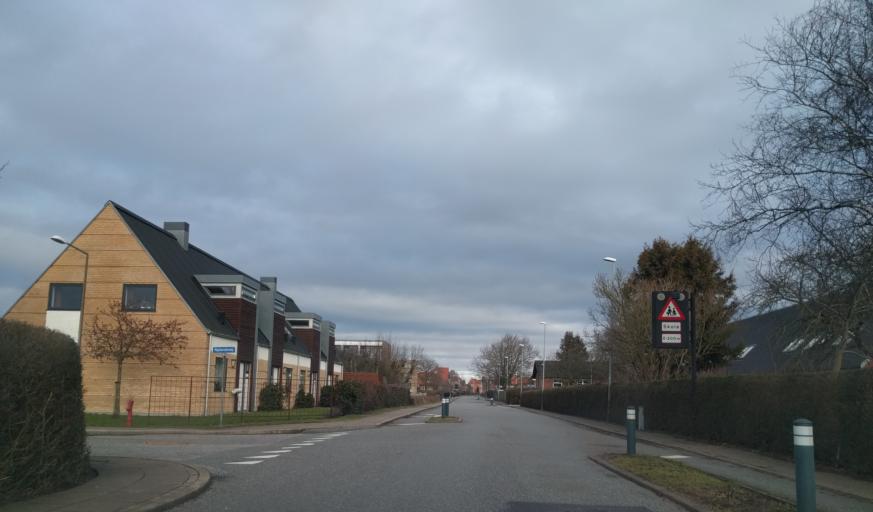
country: DK
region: North Denmark
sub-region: Alborg Kommune
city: Aalborg
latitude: 57.0270
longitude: 9.9155
